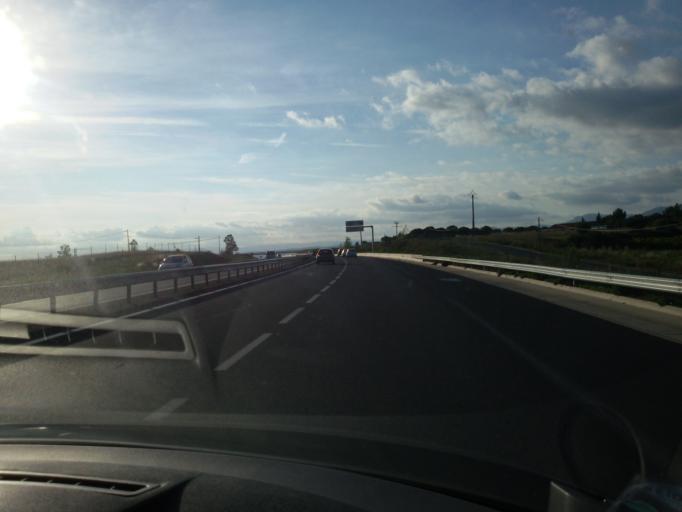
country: FR
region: Languedoc-Roussillon
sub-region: Departement de l'Herault
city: Gignac
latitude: 43.6390
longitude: 3.5785
